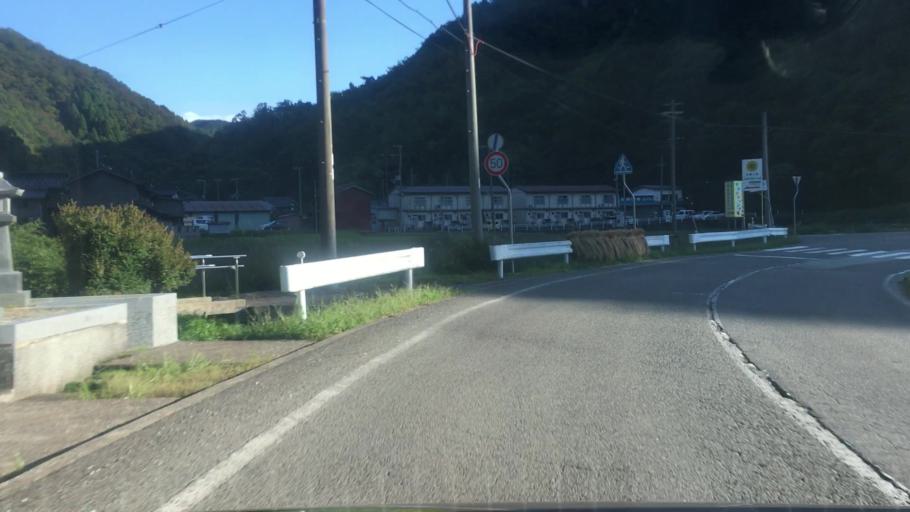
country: JP
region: Hyogo
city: Toyooka
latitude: 35.6062
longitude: 134.8082
